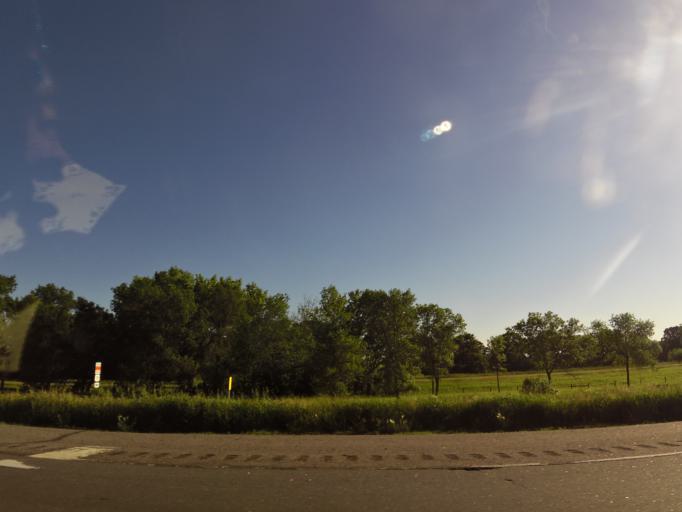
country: US
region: Minnesota
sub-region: Stearns County
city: Melrose
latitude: 45.6948
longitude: -94.8777
